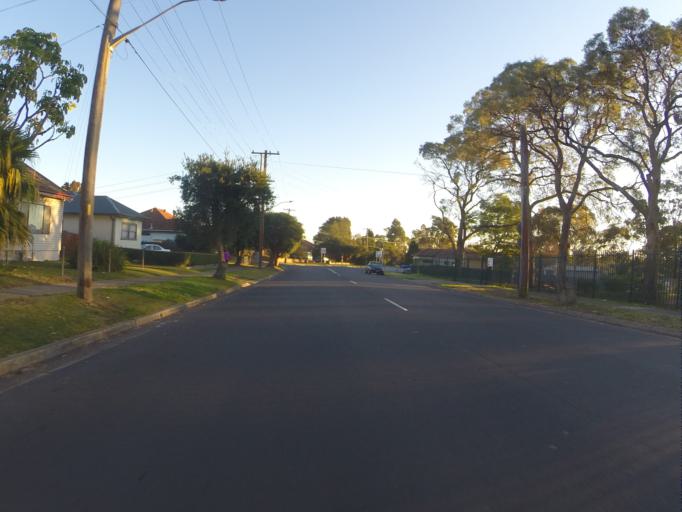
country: AU
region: New South Wales
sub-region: Sutherland Shire
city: Engadine
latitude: -34.0630
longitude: 151.0115
